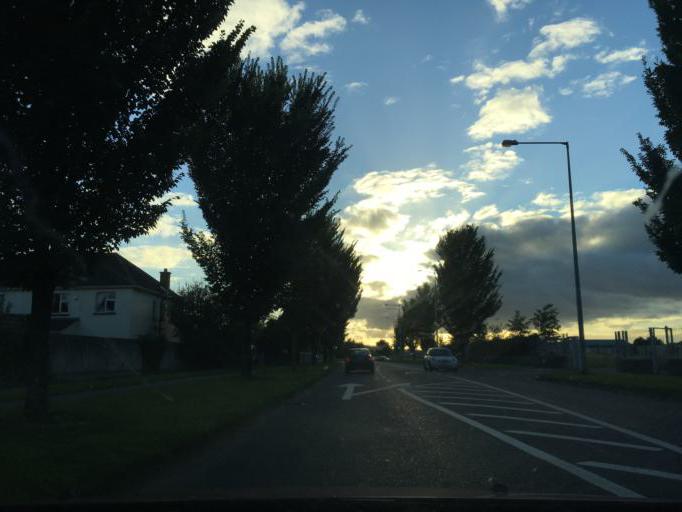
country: IE
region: Leinster
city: Firhouse
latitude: 53.2761
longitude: -6.3373
